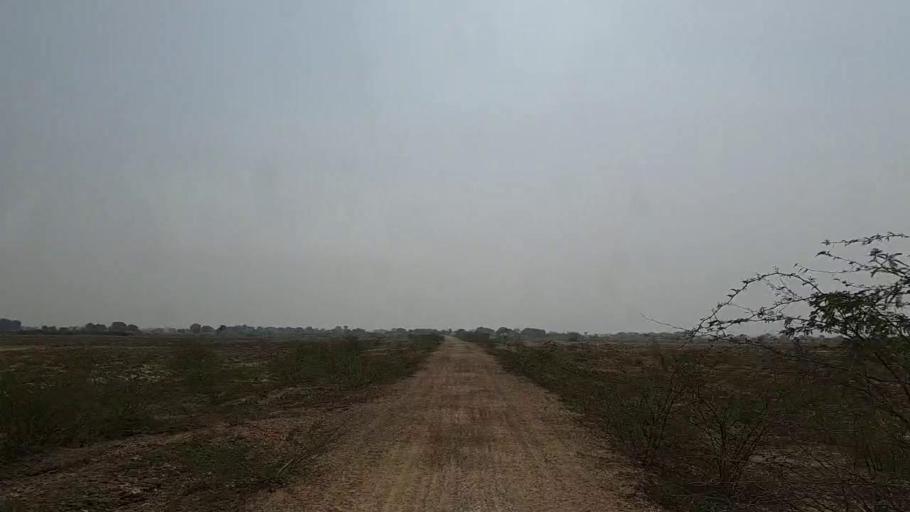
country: PK
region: Sindh
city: Naukot
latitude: 24.8092
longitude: 69.3615
